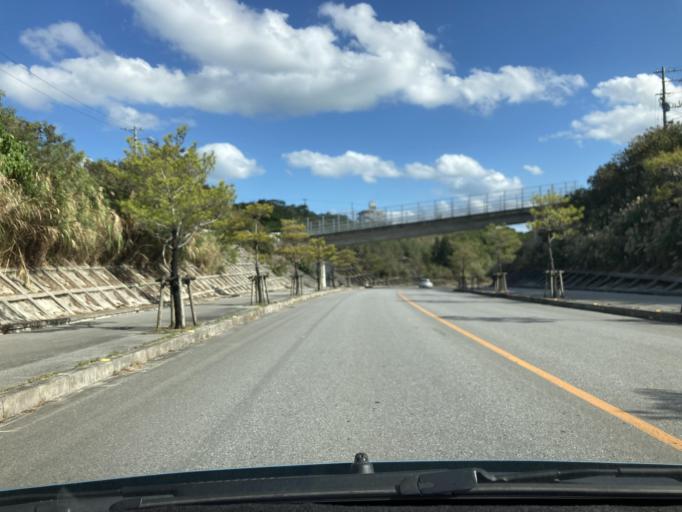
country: JP
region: Okinawa
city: Gushikawa
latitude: 26.3535
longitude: 127.8550
